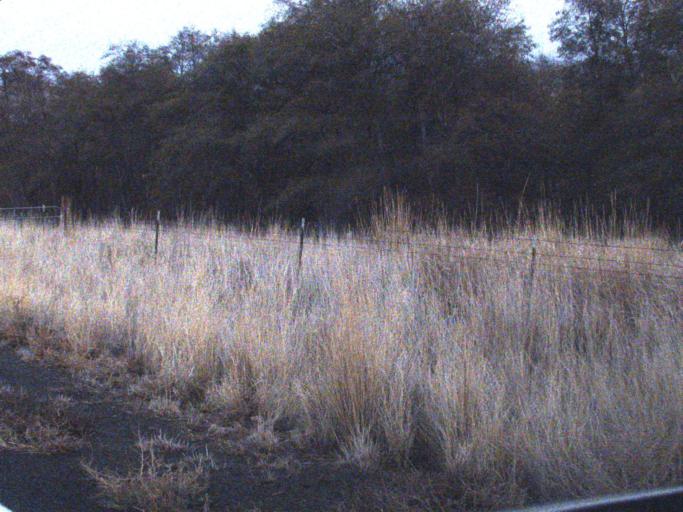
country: US
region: Washington
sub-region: Columbia County
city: Dayton
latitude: 46.5049
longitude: -118.0203
